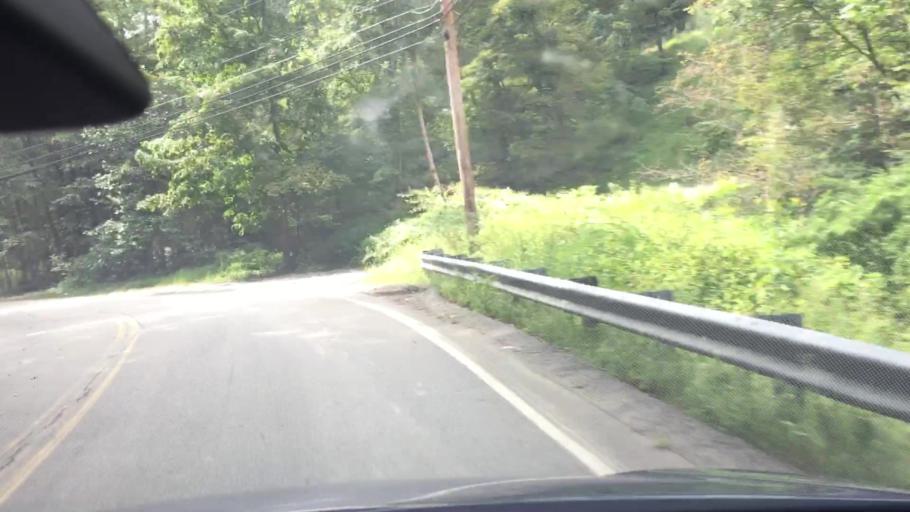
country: US
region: Pennsylvania
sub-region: Allegheny County
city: Monroeville
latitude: 40.4249
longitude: -79.7718
